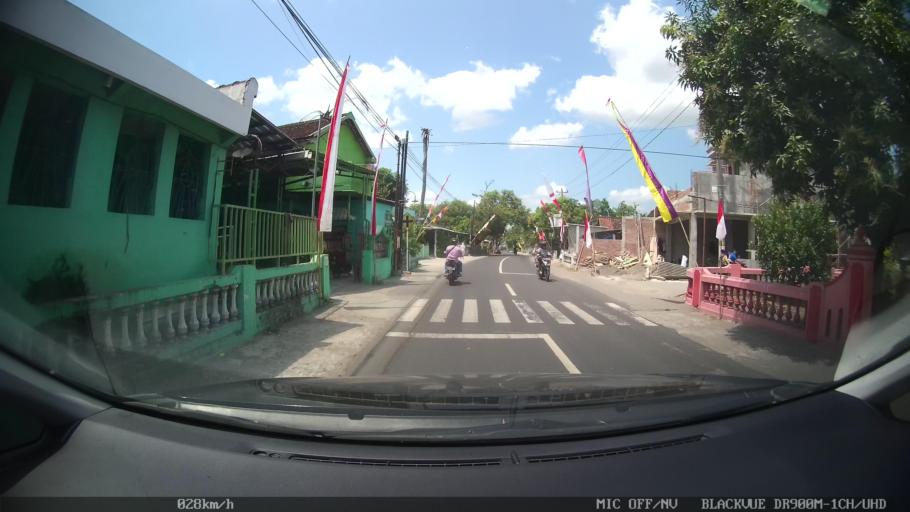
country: ID
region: Daerah Istimewa Yogyakarta
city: Sewon
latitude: -7.8732
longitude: 110.3691
